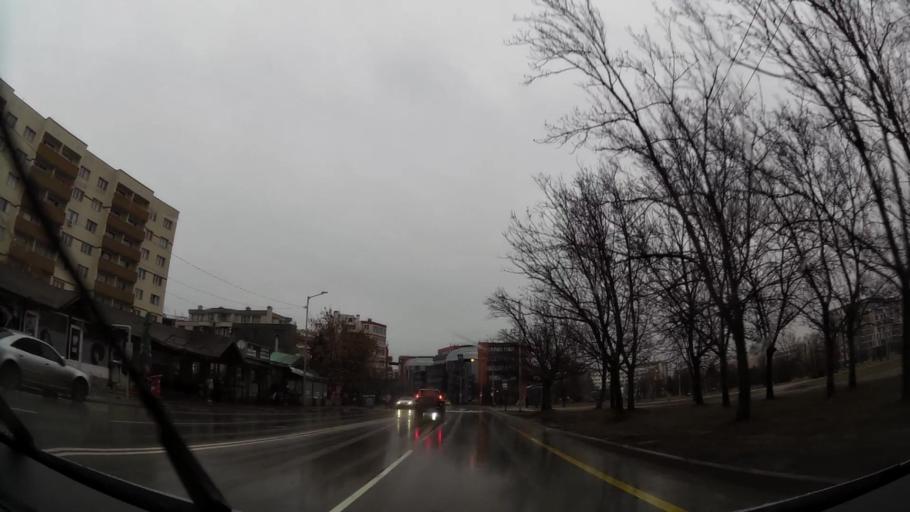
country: BG
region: Sofia-Capital
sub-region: Stolichna Obshtina
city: Sofia
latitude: 42.6556
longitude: 23.3495
